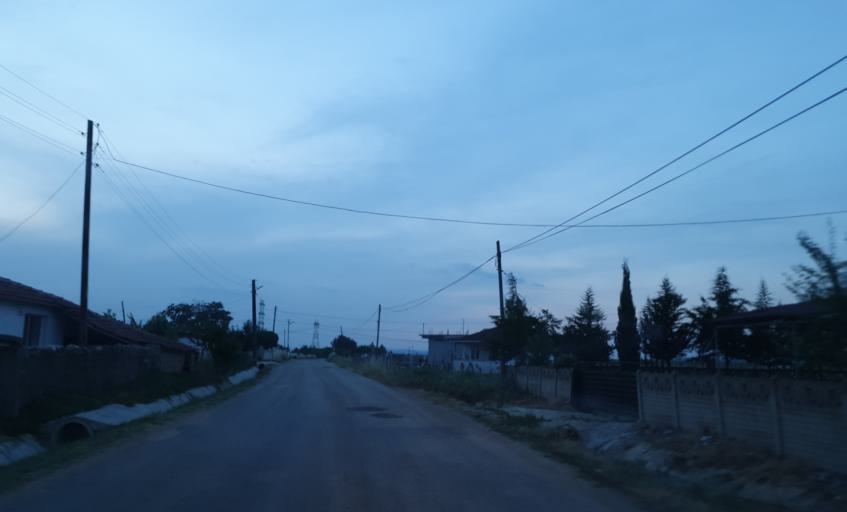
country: TR
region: Kirklareli
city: Vize
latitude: 41.4894
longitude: 27.7524
